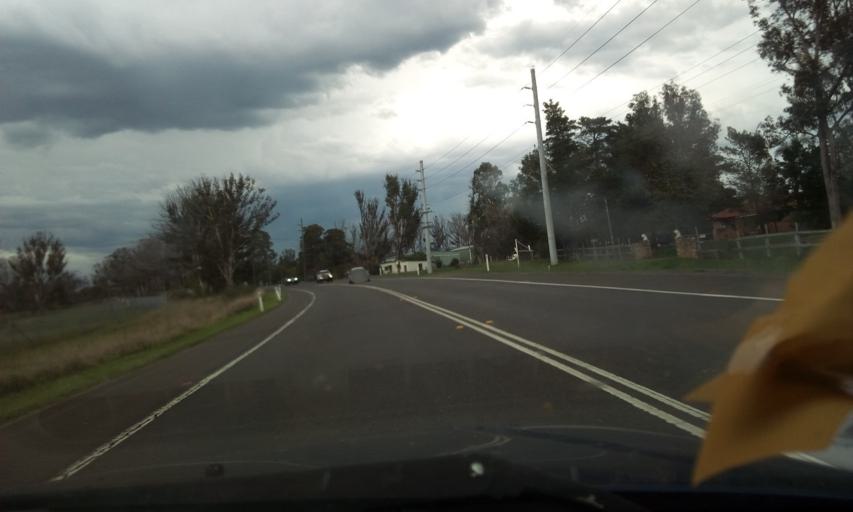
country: AU
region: New South Wales
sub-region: Penrith Municipality
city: Glenmore Park
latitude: -33.8202
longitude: 150.6860
